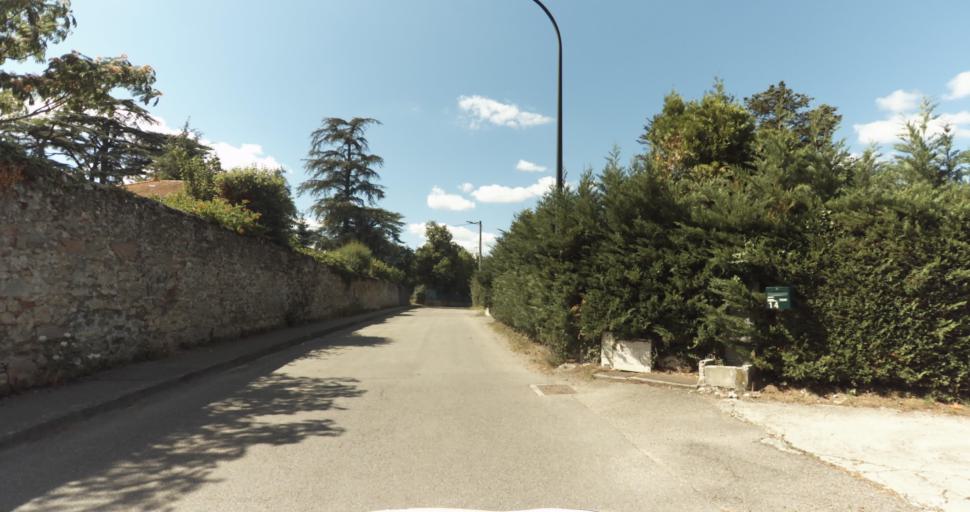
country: FR
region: Rhone-Alpes
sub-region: Departement du Rhone
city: Chaponost
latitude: 45.7164
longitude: 4.7485
